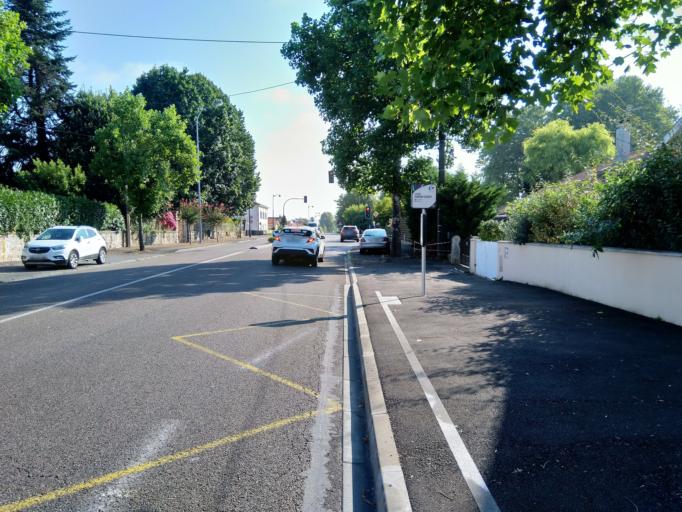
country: FR
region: Aquitaine
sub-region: Departement des Landes
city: Saint-Paul-les-Dax
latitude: 43.7264
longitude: -1.0454
